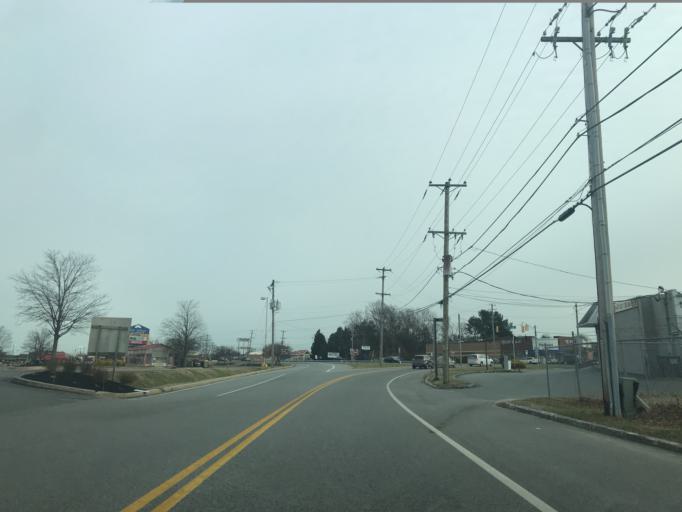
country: US
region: Maryland
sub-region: Cecil County
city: Elkton
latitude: 39.6018
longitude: -75.8050
